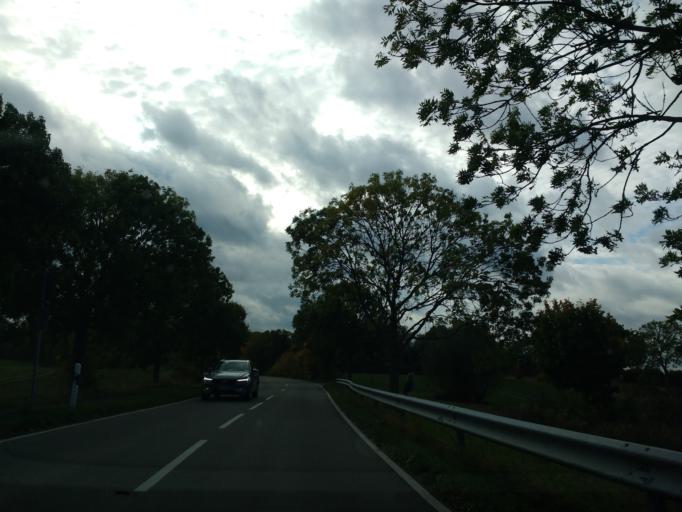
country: DE
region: Schleswig-Holstein
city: Travemuende
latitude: 53.9751
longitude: 10.8511
